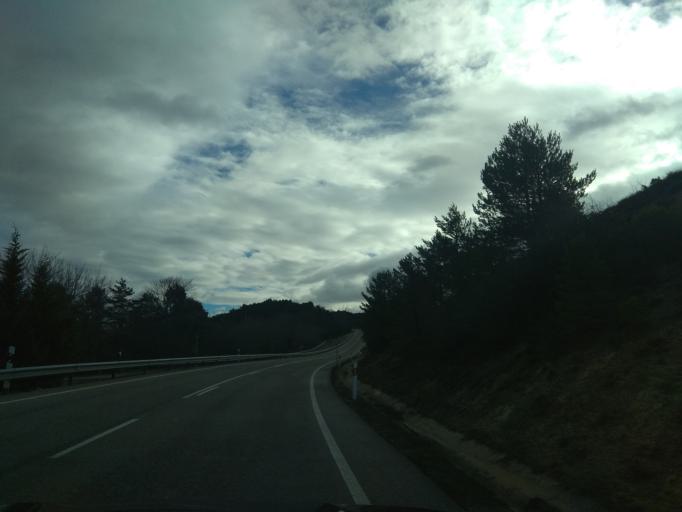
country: ES
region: Castille and Leon
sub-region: Provincia de Burgos
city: Arija
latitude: 42.9986
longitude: -3.8383
